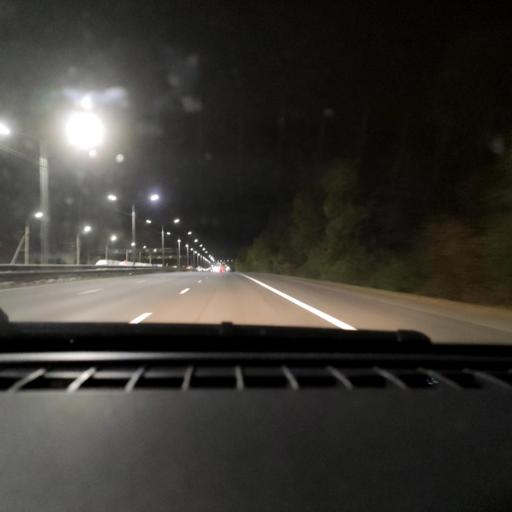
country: RU
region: Voronezj
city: Podgornoye
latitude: 51.8175
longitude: 39.2081
